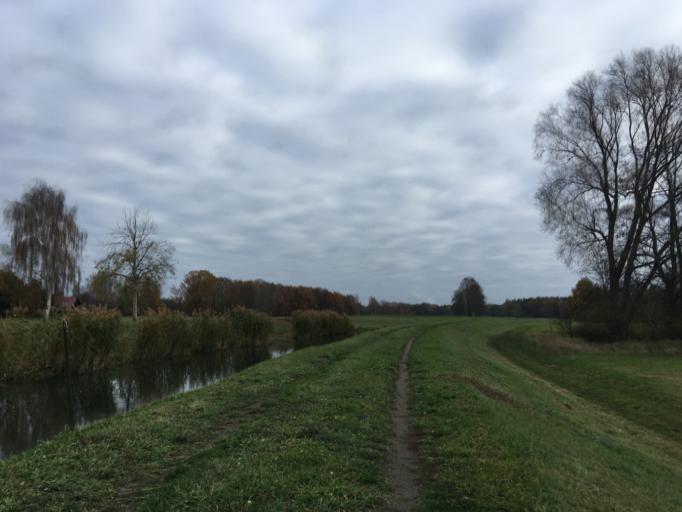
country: DE
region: Brandenburg
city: Werben
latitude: 51.8382
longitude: 14.1946
